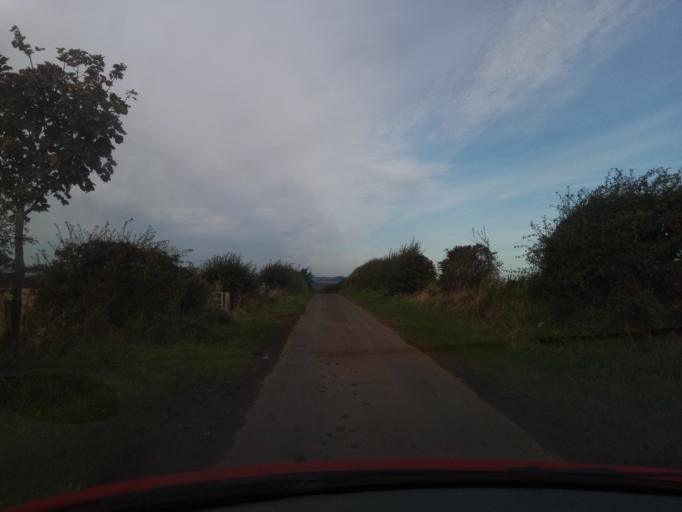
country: GB
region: Scotland
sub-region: The Scottish Borders
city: Kelso
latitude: 55.5892
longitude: -2.3801
